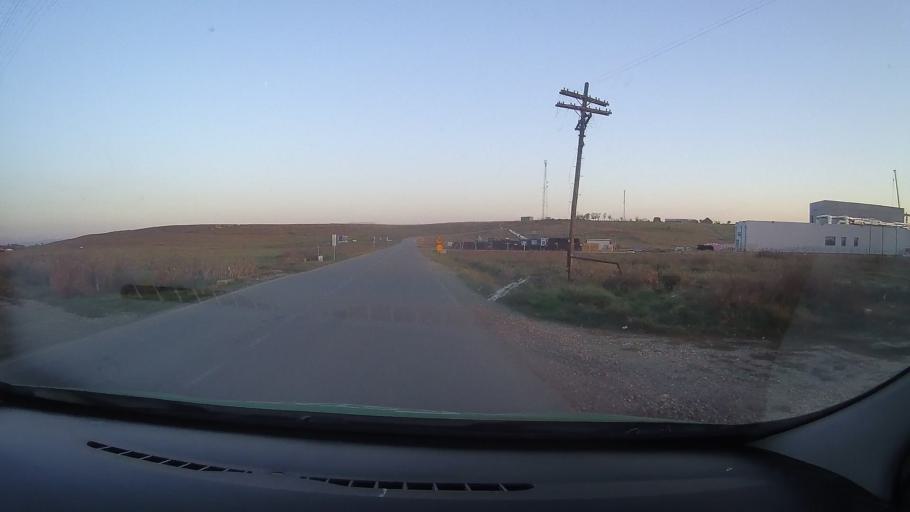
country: RO
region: Timis
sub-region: Comuna Manastiur
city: Manastiur
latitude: 45.8277
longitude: 22.0694
